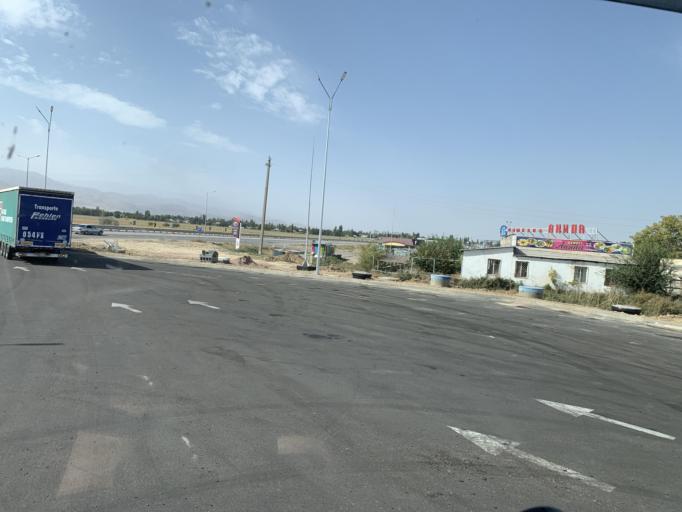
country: KZ
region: Zhambyl
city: Merke
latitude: 42.8751
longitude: 73.1304
